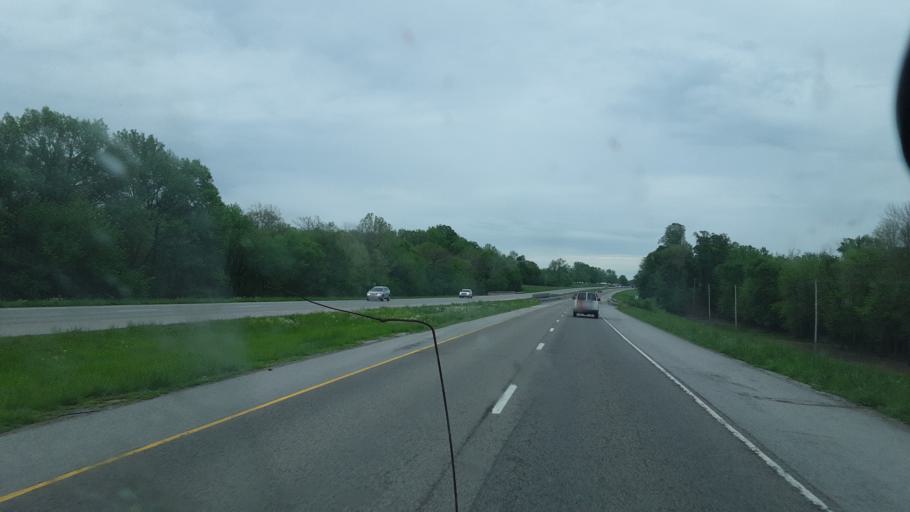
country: US
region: Illinois
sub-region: Jackson County
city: Murphysboro
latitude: 37.7646
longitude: -89.2921
